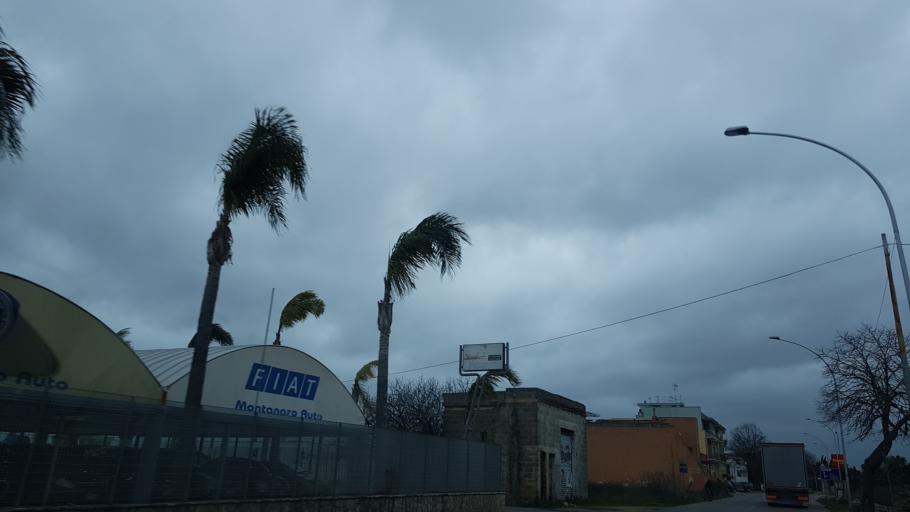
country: IT
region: Apulia
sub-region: Provincia di Brindisi
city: San Vito dei Normanni
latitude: 40.6575
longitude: 17.7206
